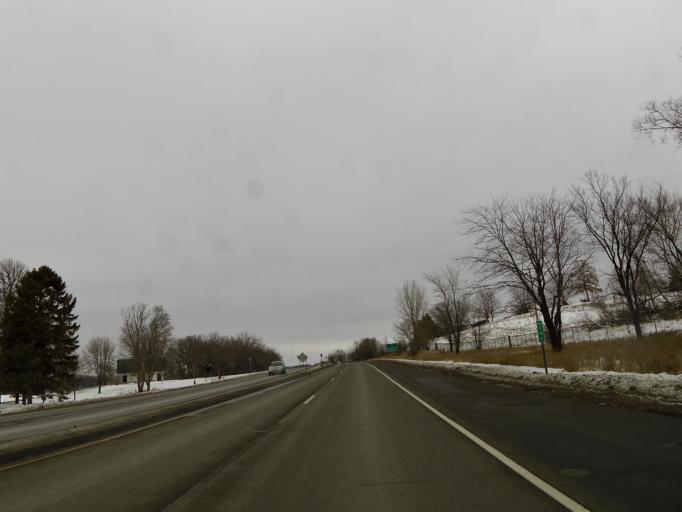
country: US
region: Minnesota
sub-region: Ramsey County
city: Little Canada
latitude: 45.0036
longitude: -93.0608
